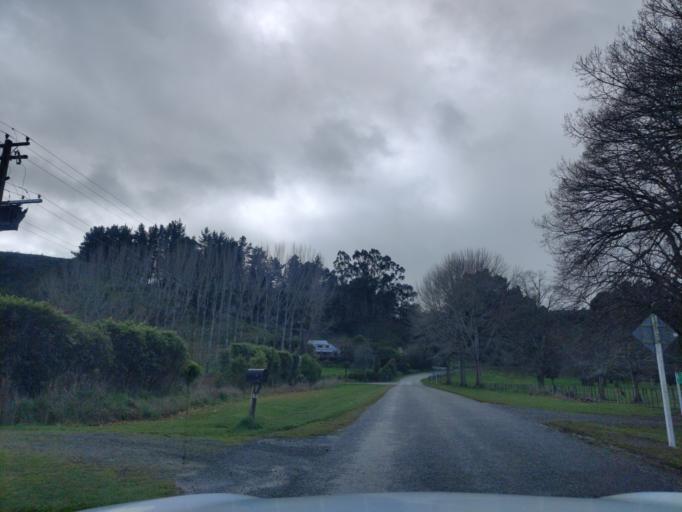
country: NZ
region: Manawatu-Wanganui
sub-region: Palmerston North City
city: Palmerston North
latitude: -40.1685
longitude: 175.8015
